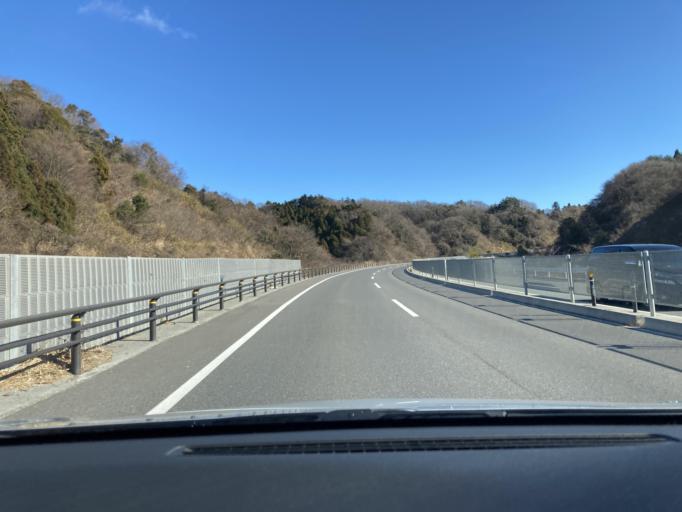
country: JP
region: Fukushima
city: Iwaki
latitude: 37.0368
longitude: 140.9166
